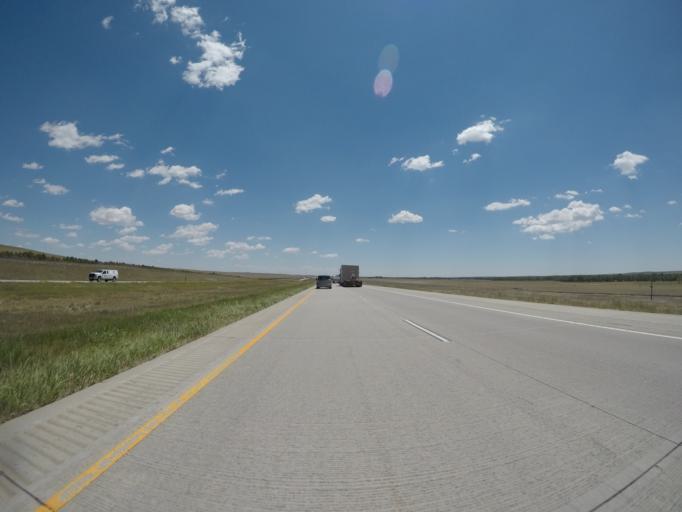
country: US
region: Colorado
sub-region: Lincoln County
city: Limon
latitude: 39.2805
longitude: -103.7682
